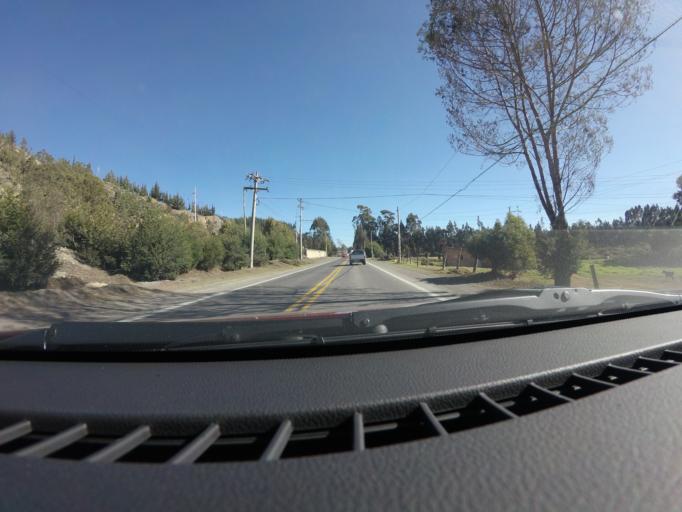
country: CO
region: Cundinamarca
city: Ubate
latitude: 5.2872
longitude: -73.8196
